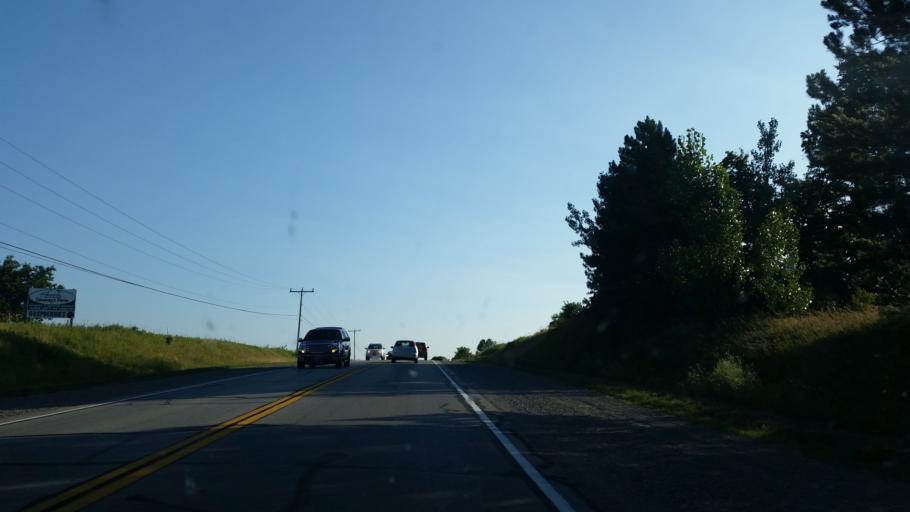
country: CA
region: Ontario
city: Brampton
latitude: 43.7977
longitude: -79.8511
